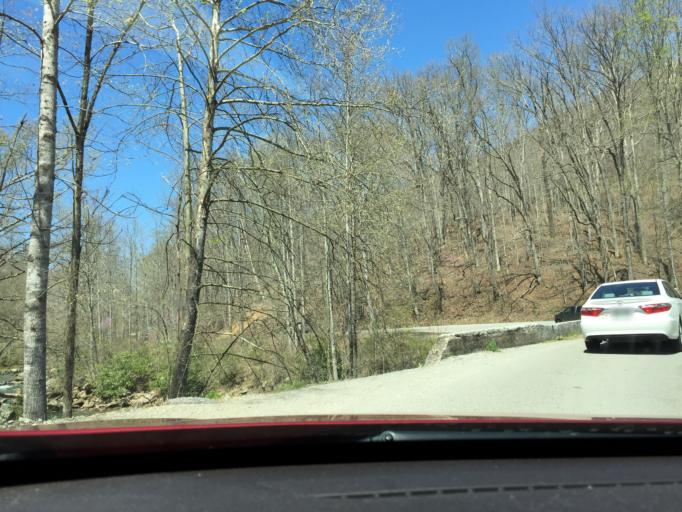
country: US
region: Tennessee
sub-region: Campbell County
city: Caryville
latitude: 36.3525
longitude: -84.2617
